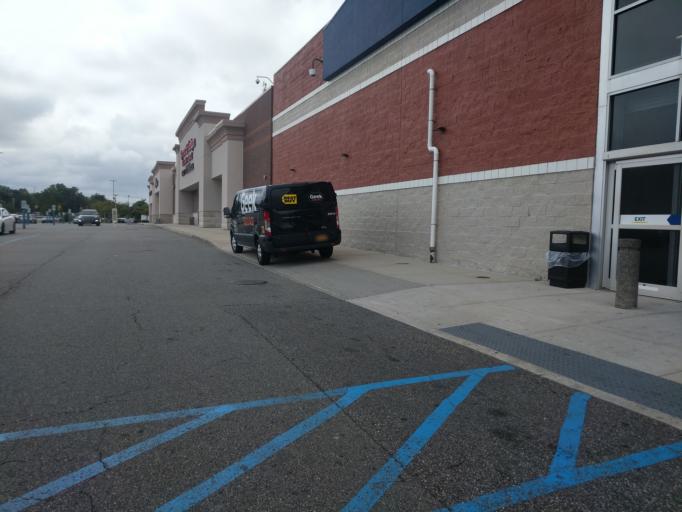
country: US
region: New York
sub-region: Nassau County
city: South Valley Stream
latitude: 40.6640
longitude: -73.7236
